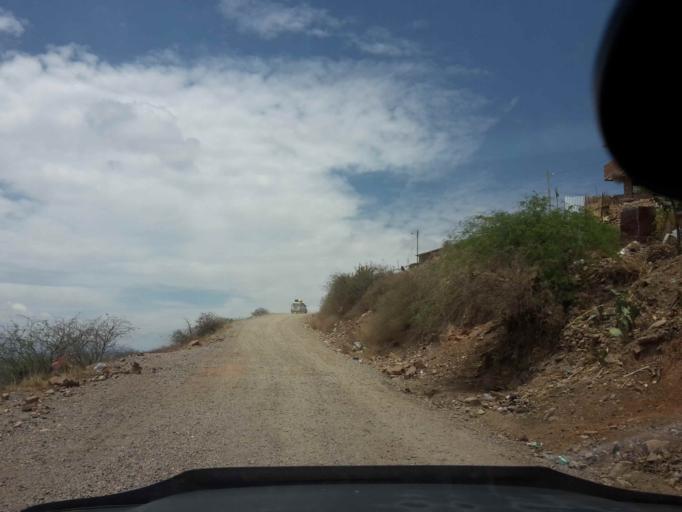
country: BO
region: Cochabamba
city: Sipe Sipe
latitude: -17.5676
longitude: -66.3491
